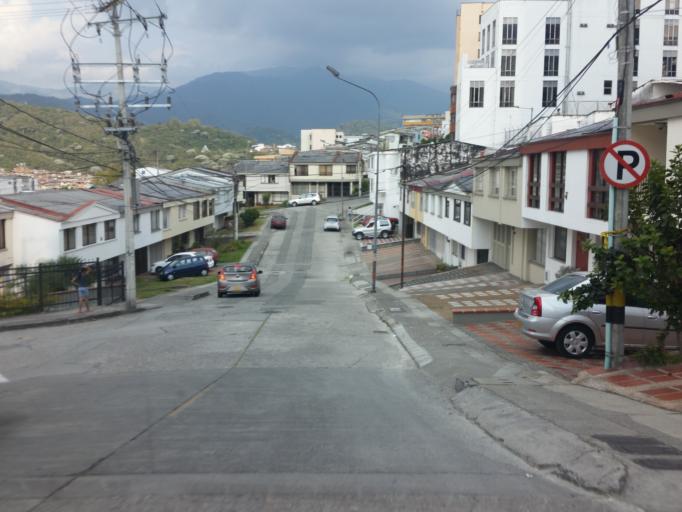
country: CO
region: Caldas
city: Manizales
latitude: 5.0628
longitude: -75.4947
